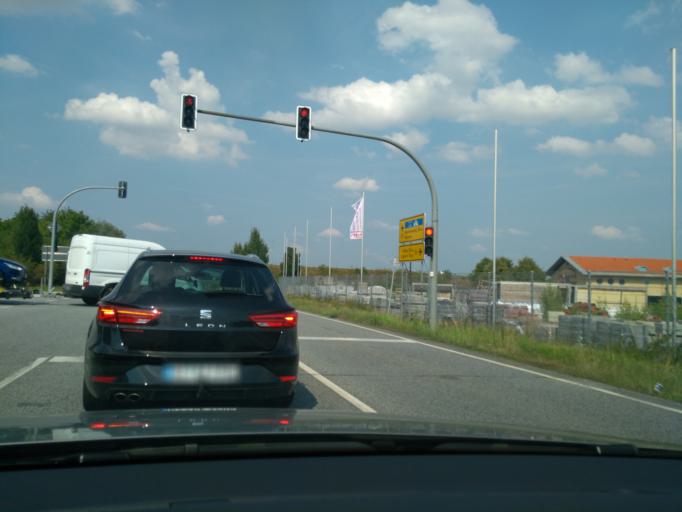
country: DE
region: Saxony
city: Bautzen
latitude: 51.1811
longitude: 14.4102
